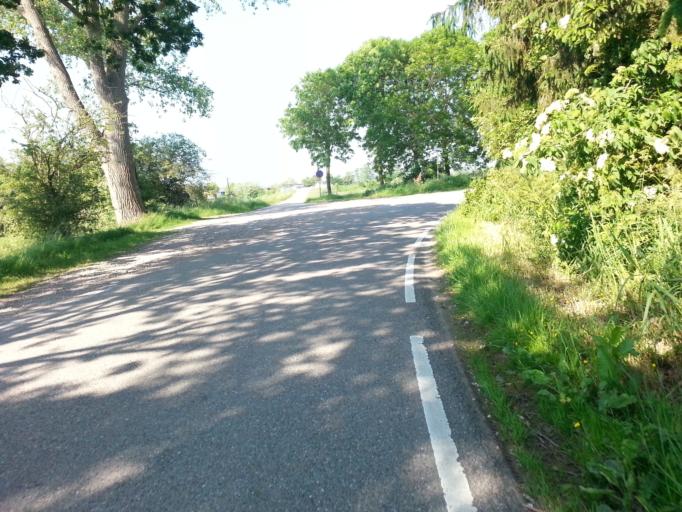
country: NL
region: Utrecht
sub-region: Gemeente Utrechtse Heuvelrug
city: Driebergen-Rijsenburg
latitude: 52.0221
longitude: 5.2666
